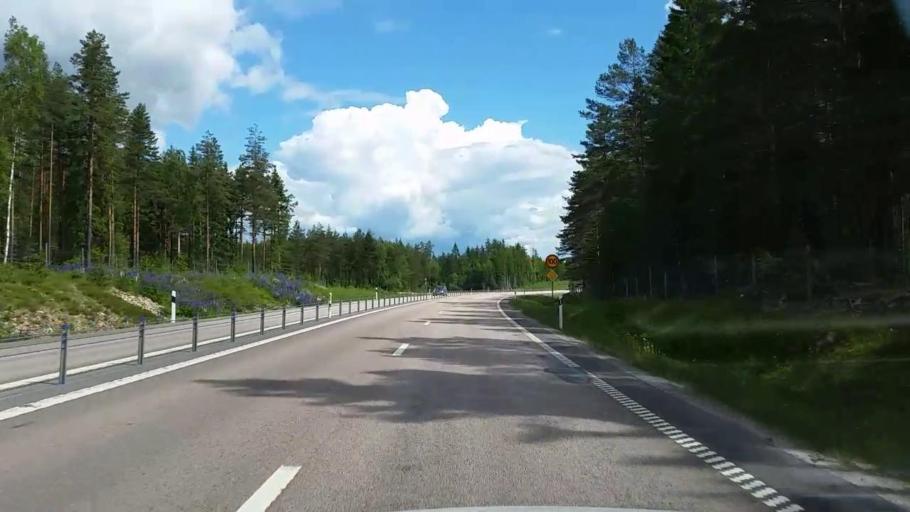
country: SE
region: Dalarna
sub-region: Avesta Kommun
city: Avesta
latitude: 60.1111
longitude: 16.0452
